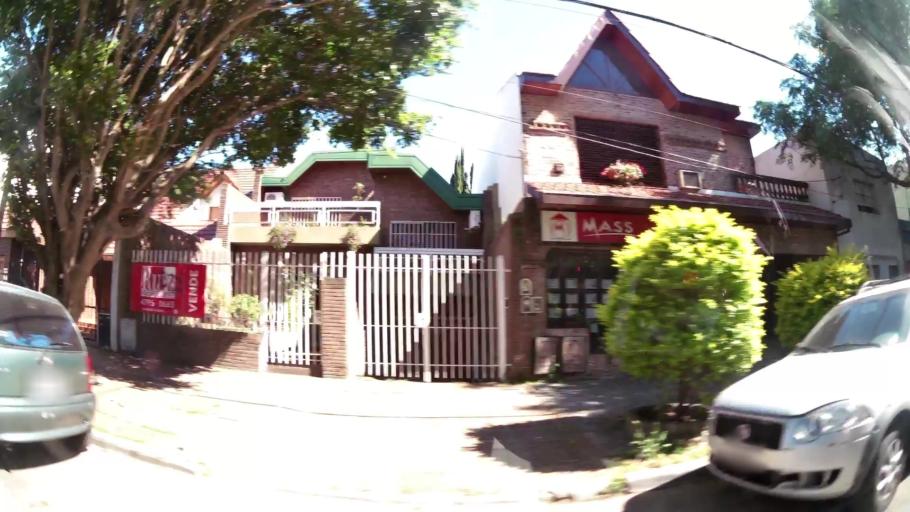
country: AR
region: Buenos Aires
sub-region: Partido de Vicente Lopez
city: Olivos
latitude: -34.5380
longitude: -58.4834
